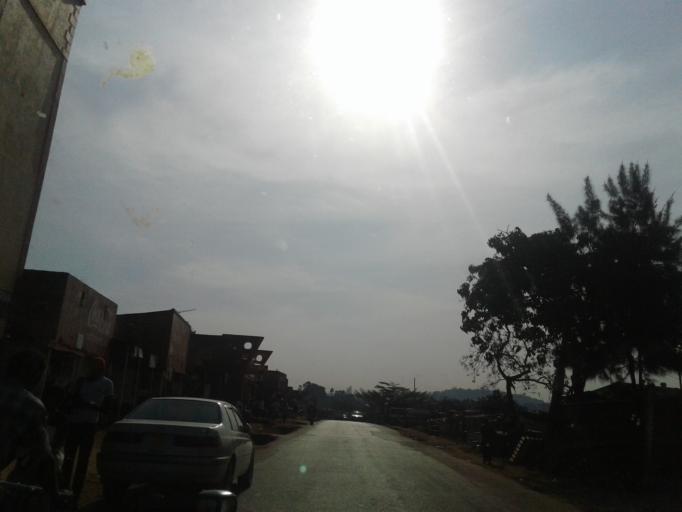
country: UG
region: Central Region
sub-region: Wakiso District
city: Kireka
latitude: 0.3335
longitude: 32.6260
